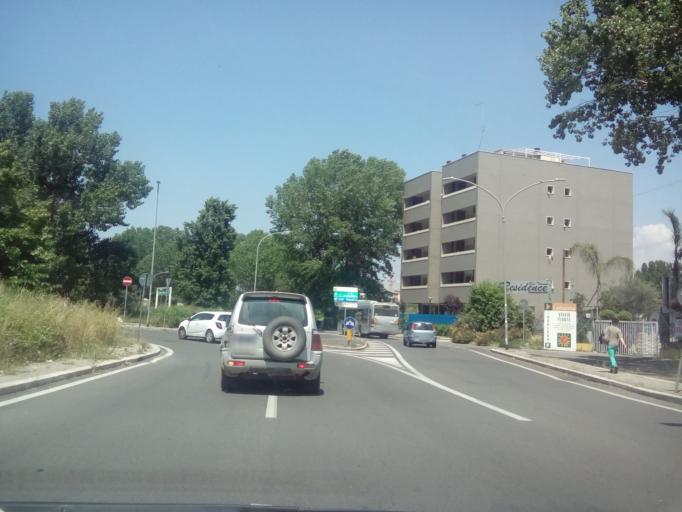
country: IT
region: Latium
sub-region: Citta metropolitana di Roma Capitale
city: Vitinia
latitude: 41.8097
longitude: 12.4537
